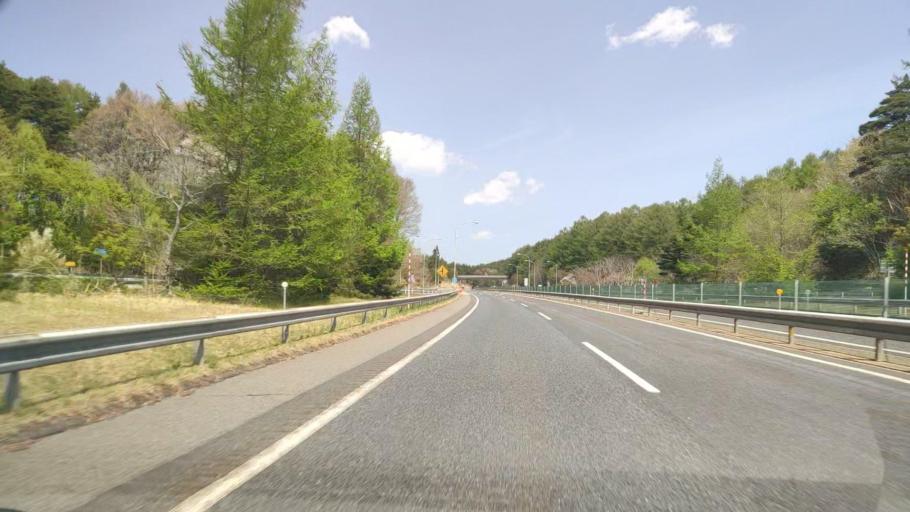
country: JP
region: Iwate
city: Ichinohe
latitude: 40.2975
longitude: 141.4231
